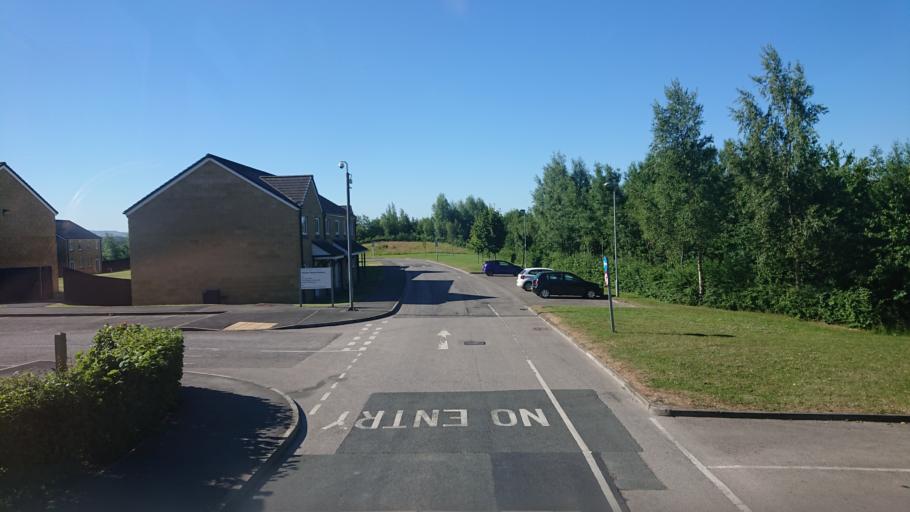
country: GB
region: England
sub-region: Lancashire
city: Galgate
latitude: 54.0037
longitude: -2.7903
